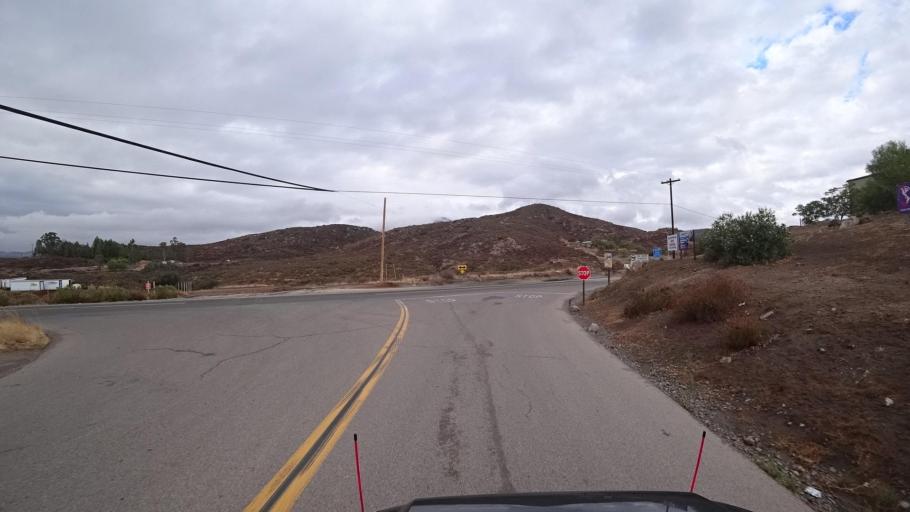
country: MX
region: Baja California
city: Tecate
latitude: 32.5828
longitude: -116.6329
